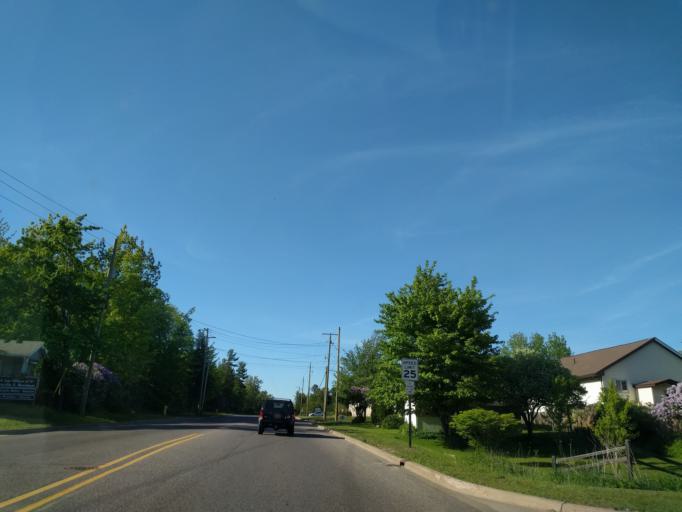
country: US
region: Michigan
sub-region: Marquette County
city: Trowbridge Park
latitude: 46.5483
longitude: -87.4198
